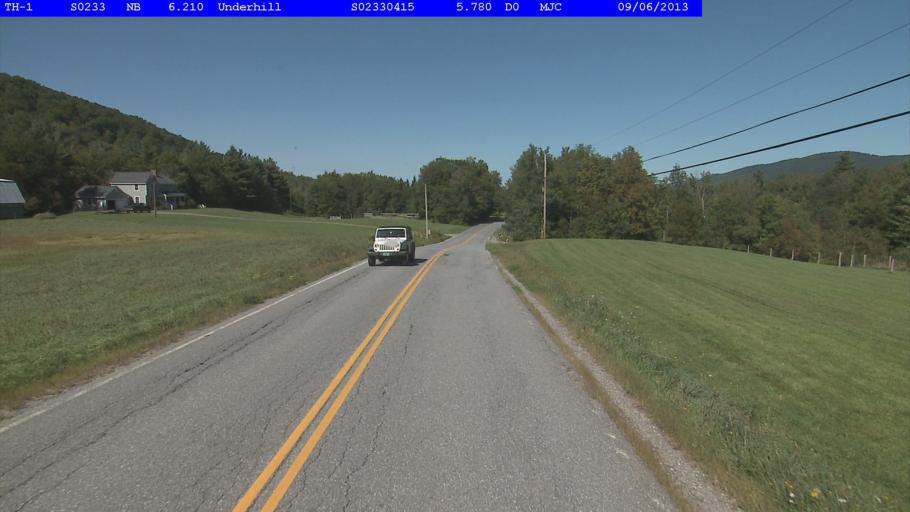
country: US
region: Vermont
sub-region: Chittenden County
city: Jericho
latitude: 44.5483
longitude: -72.8678
